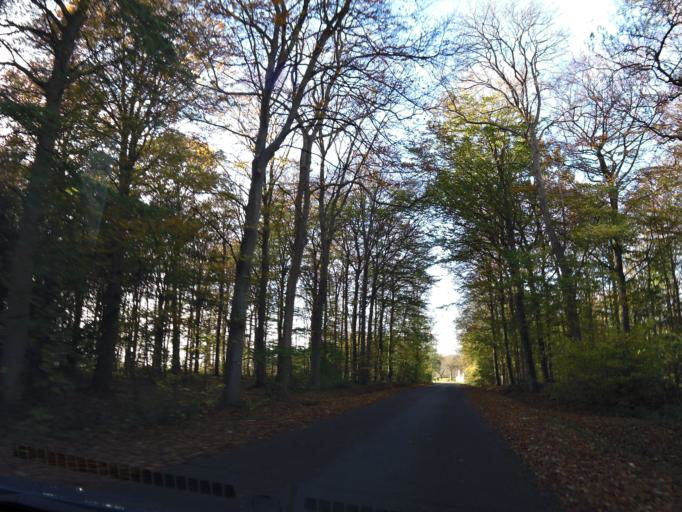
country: DK
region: Central Jutland
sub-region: Odder Kommune
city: Odder
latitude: 55.9140
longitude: 10.2462
